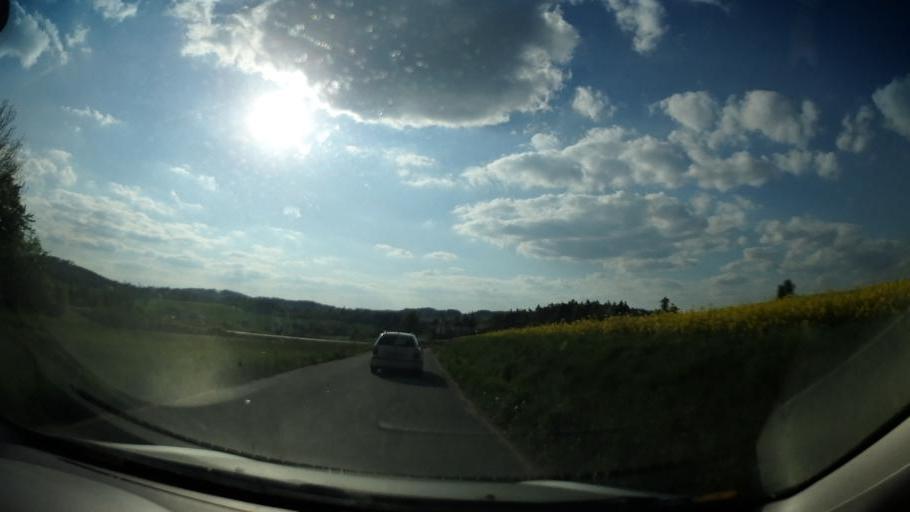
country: CZ
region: Vysocina
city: Budisov
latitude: 49.3134
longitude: 15.9726
